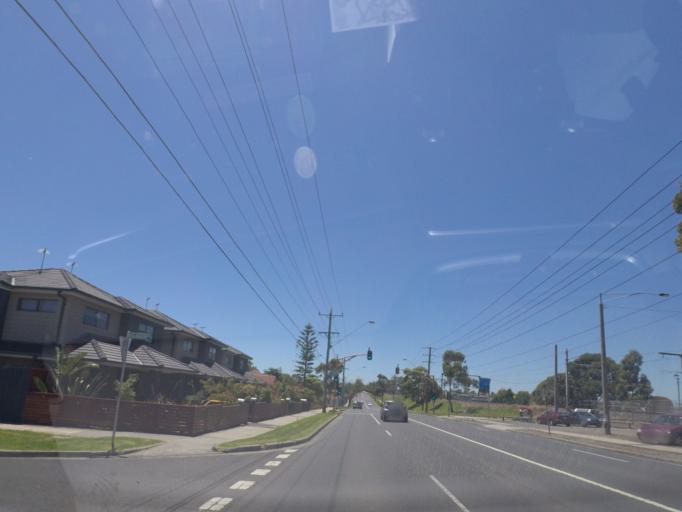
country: AU
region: Victoria
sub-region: Darebin
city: Reservoir
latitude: -37.7079
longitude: 145.0091
